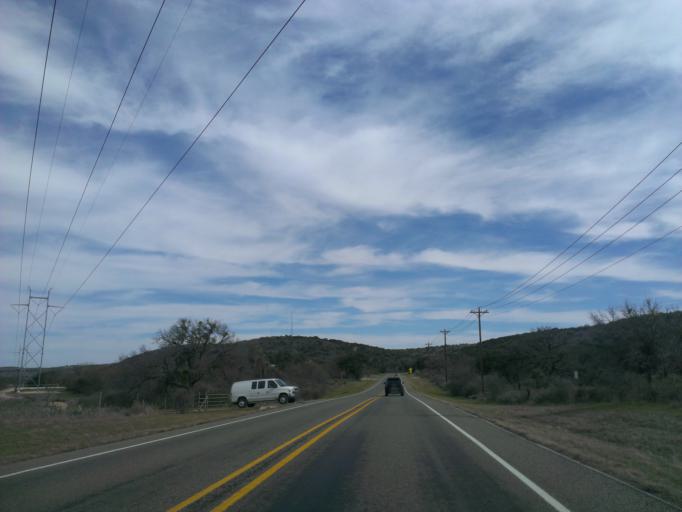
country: US
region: Texas
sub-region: Llano County
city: Kingsland
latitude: 30.6709
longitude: -98.4000
